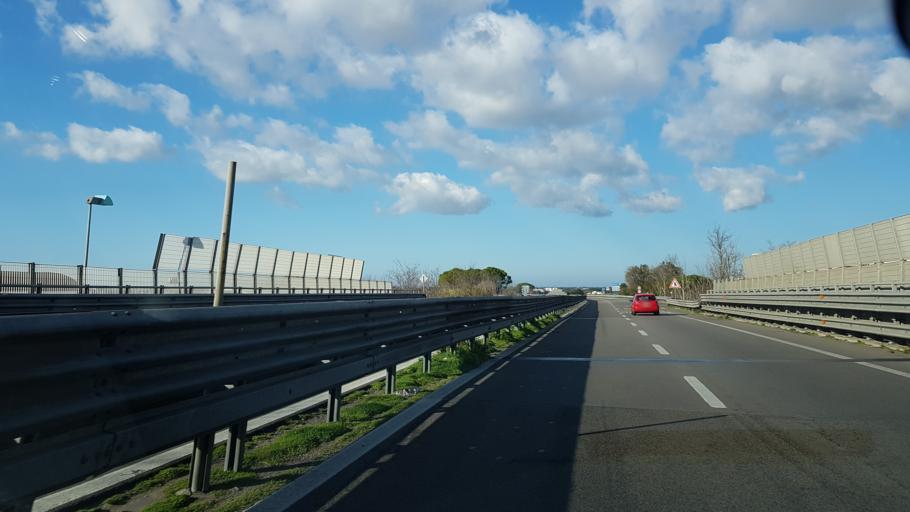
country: IT
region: Apulia
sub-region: Provincia di Lecce
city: Castromediano
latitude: 40.3253
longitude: 18.1653
